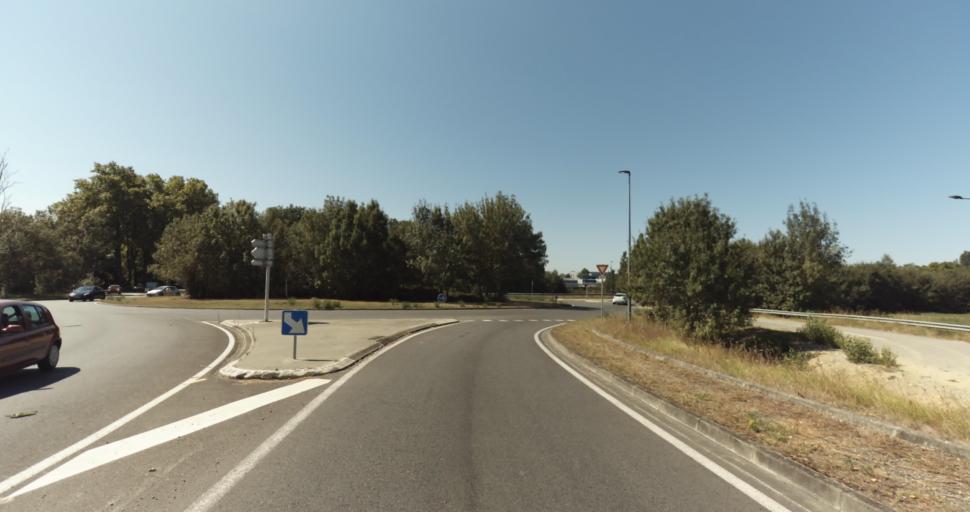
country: FR
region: Midi-Pyrenees
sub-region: Departement de la Haute-Garonne
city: Montrabe
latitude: 43.6429
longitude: 1.5050
